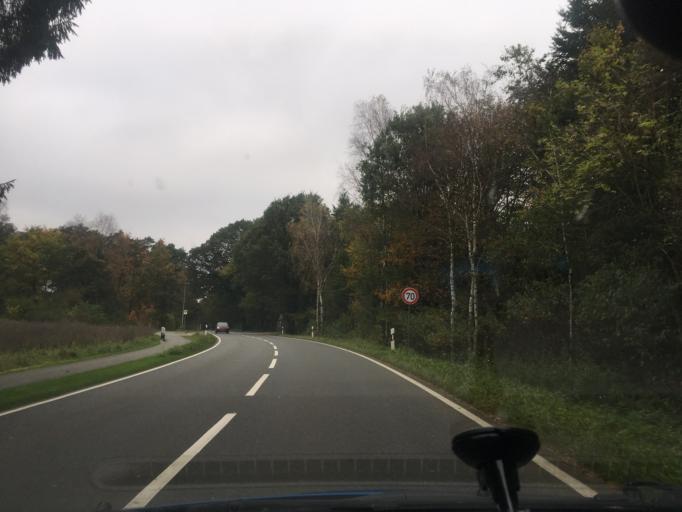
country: DE
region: Lower Saxony
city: Bispingen
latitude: 53.0677
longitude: 9.9957
